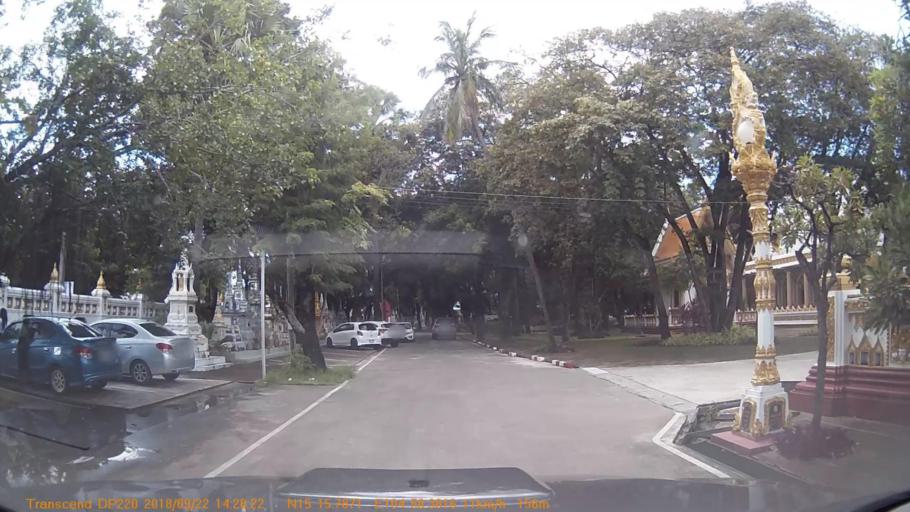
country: TH
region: Changwat Ubon Ratchathani
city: Ubon Ratchathani
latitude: 15.2631
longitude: 104.8396
